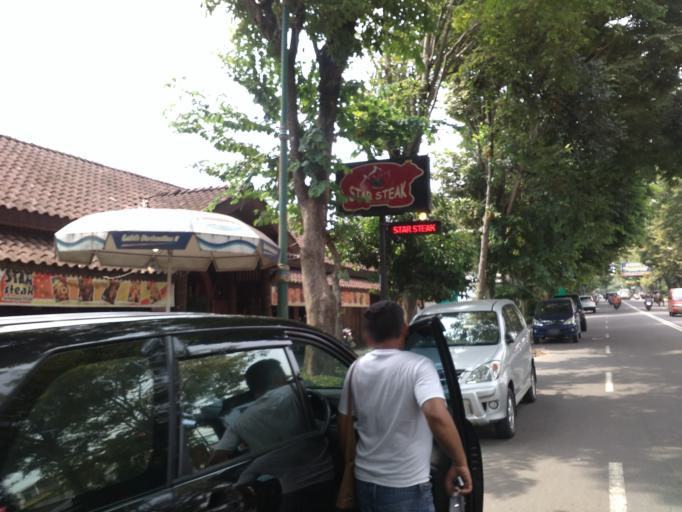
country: ID
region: Central Java
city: Boyolali
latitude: -7.5258
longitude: 110.6003
